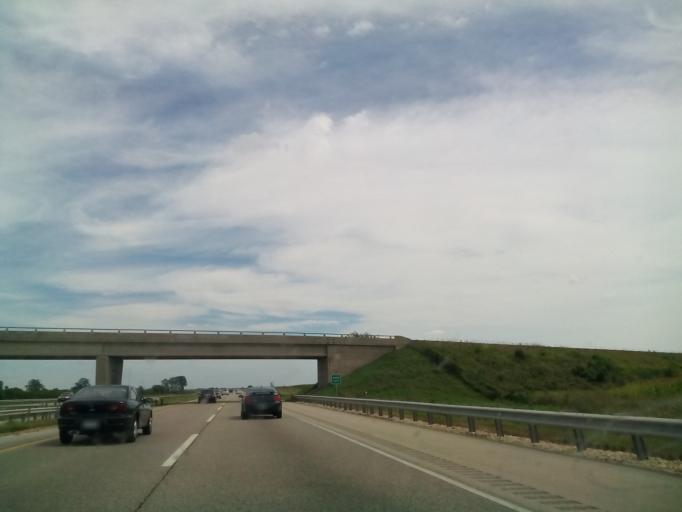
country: US
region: Illinois
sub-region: Kane County
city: Maple Park
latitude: 41.8644
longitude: -88.5625
